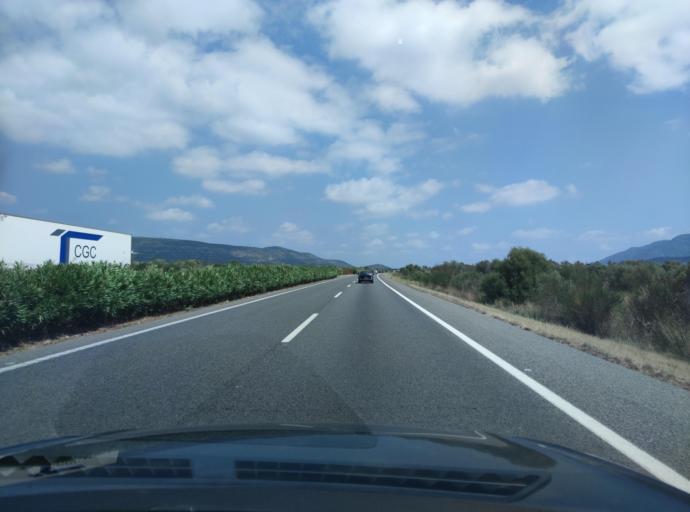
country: ES
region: Catalonia
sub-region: Provincia de Tarragona
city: Ulldecona
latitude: 40.6060
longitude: 0.4745
